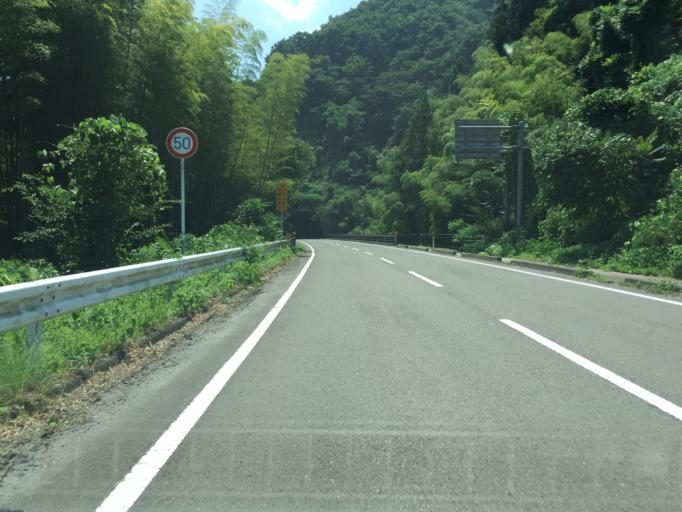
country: JP
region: Miyagi
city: Marumori
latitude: 37.9361
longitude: 140.6947
